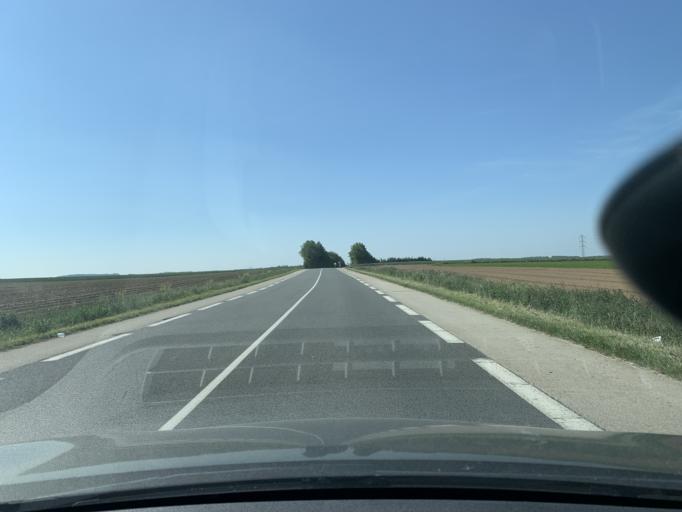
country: FR
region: Nord-Pas-de-Calais
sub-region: Departement du Nord
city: Rumilly-en-Cambresis
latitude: 50.1191
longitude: 3.2460
